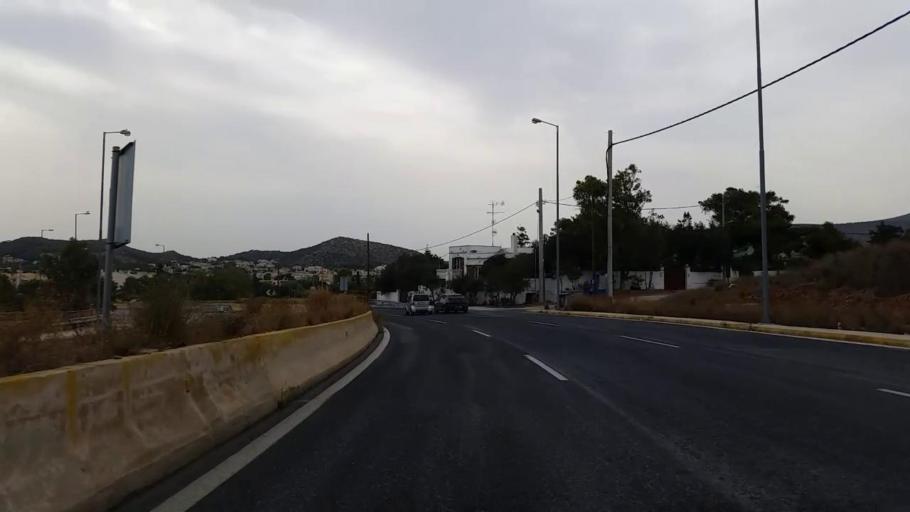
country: GR
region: Attica
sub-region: Nomarchia Anatolikis Attikis
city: Vari
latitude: 37.8225
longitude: 23.8161
